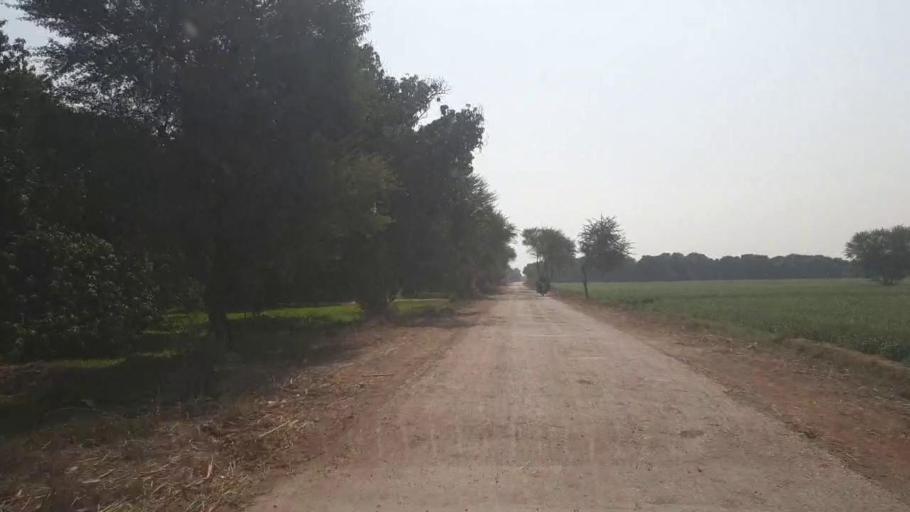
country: PK
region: Sindh
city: Tando Allahyar
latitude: 25.4810
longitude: 68.8260
